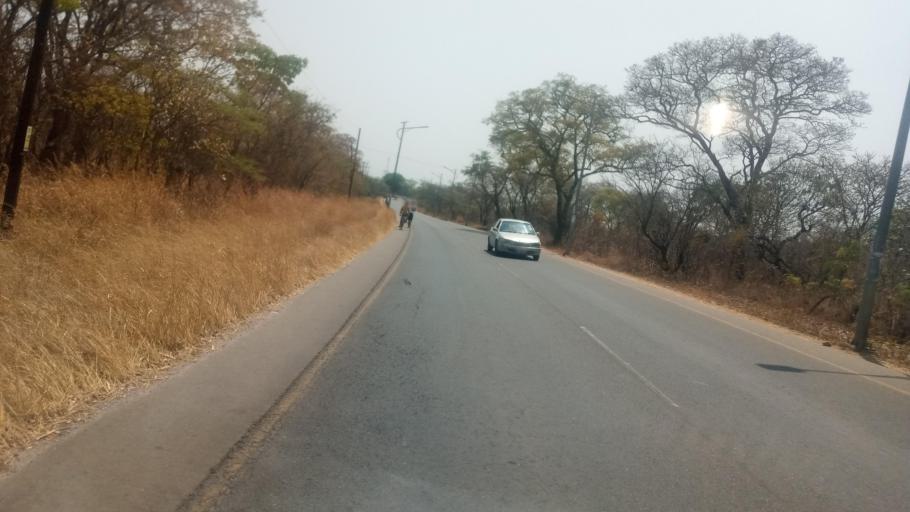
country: ZM
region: Lusaka
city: Lusaka
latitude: -15.4716
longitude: 28.4262
